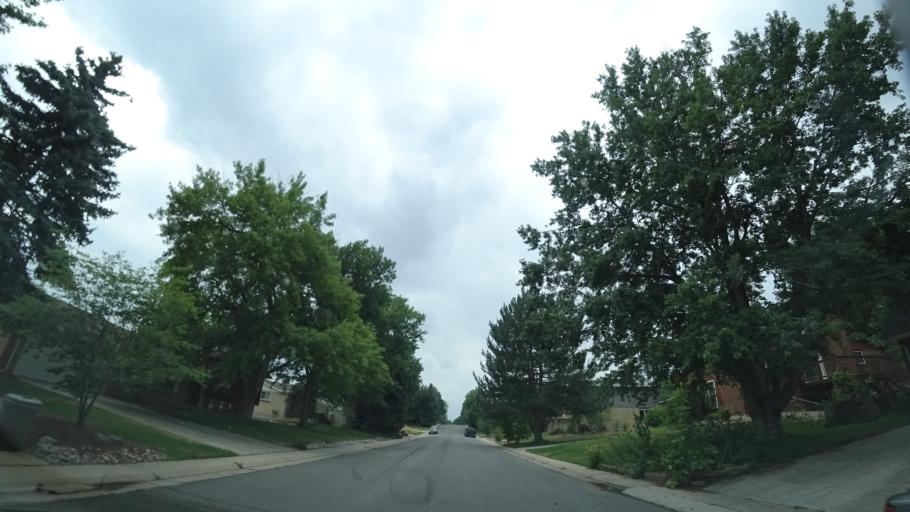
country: US
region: Colorado
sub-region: Jefferson County
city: West Pleasant View
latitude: 39.7009
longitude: -105.1487
